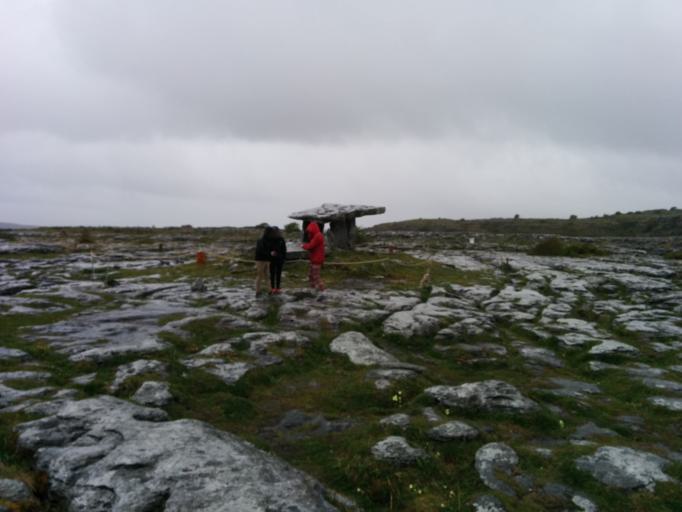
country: IE
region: Connaught
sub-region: County Galway
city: Bearna
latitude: 53.0485
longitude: -9.1399
